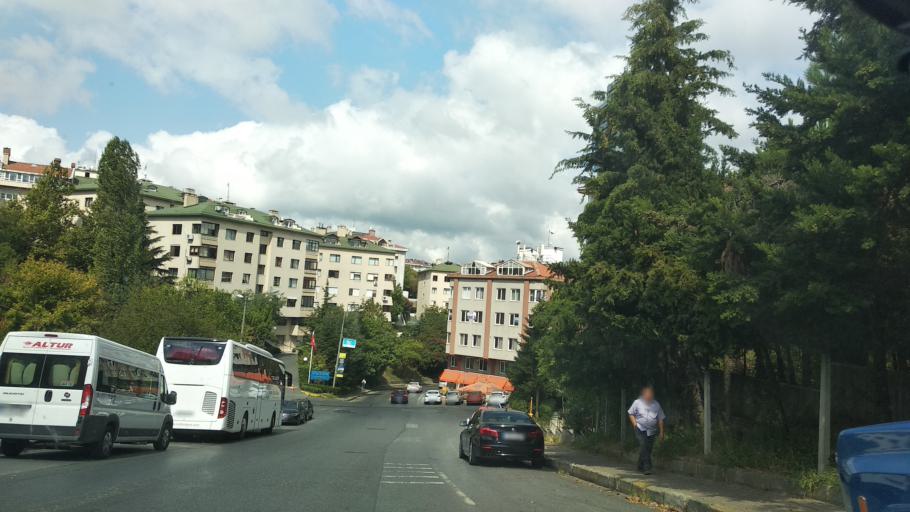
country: TR
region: Istanbul
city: Sisli
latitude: 41.0865
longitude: 29.0365
